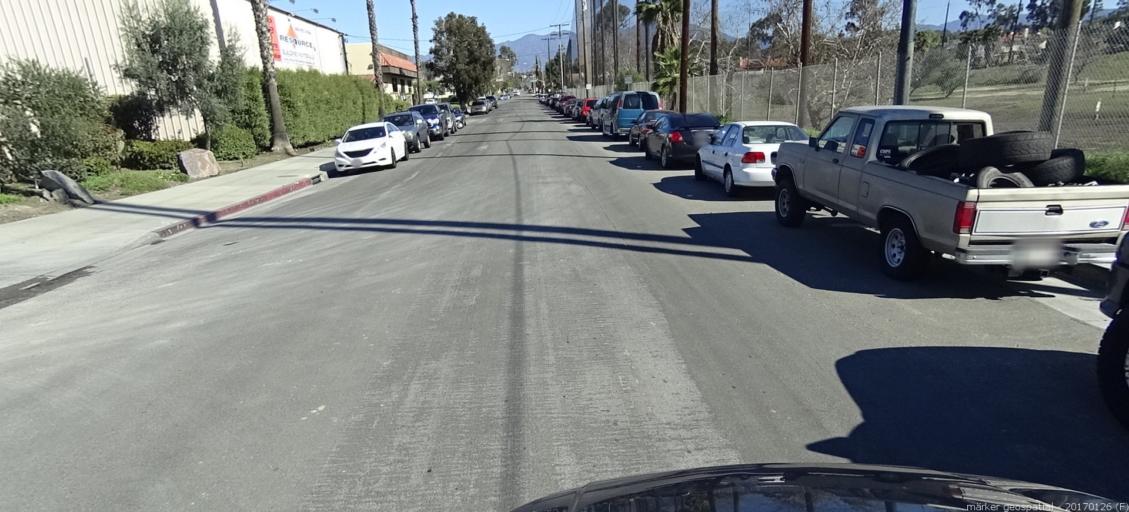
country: US
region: California
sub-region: Orange County
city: Lake Forest
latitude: 33.6249
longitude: -117.6897
